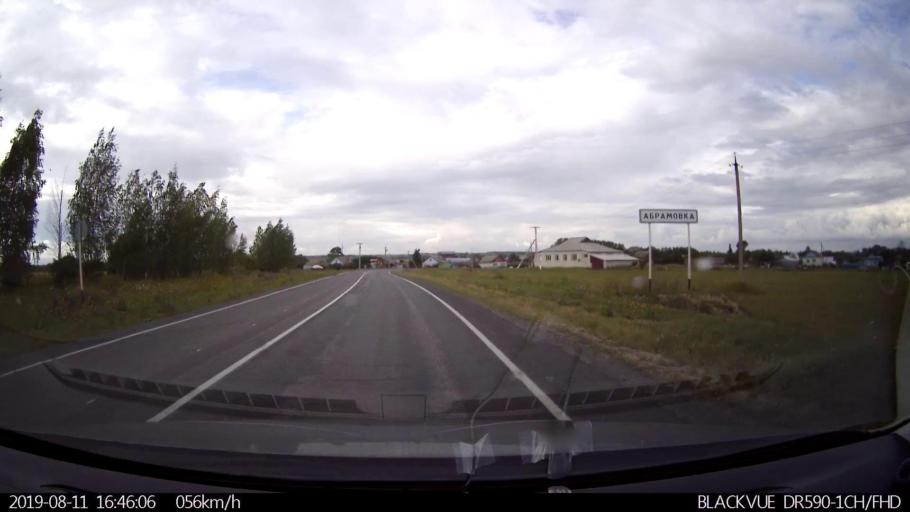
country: RU
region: Ulyanovsk
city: Mayna
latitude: 54.1959
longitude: 47.6875
